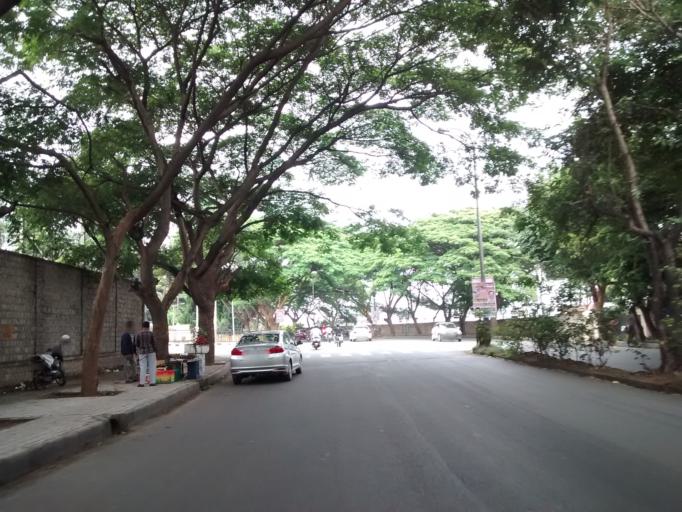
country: IN
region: Karnataka
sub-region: Bangalore Urban
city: Bangalore
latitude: 12.9547
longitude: 77.6796
